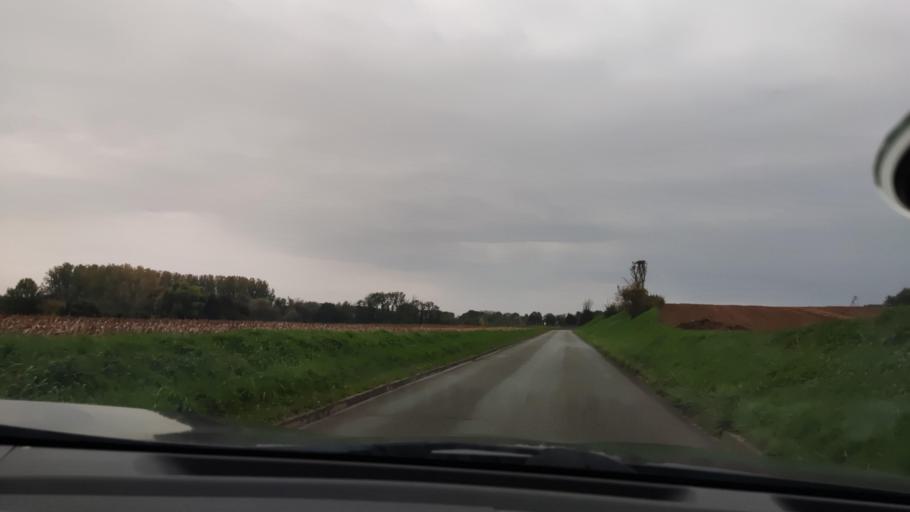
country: BE
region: Flanders
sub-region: Provincie Vlaams-Brabant
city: Hoegaarden
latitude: 50.7547
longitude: 4.8720
